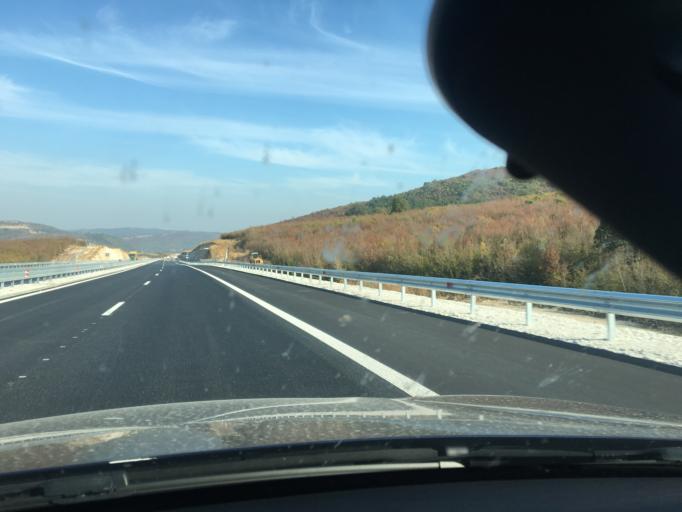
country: BG
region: Lovech
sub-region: Obshtina Yablanitsa
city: Yablanitsa
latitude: 43.0526
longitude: 24.1881
